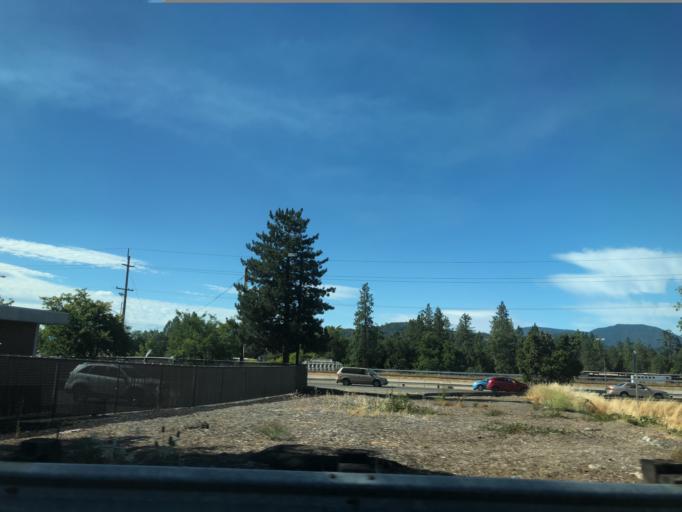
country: US
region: Oregon
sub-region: Josephine County
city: Grants Pass
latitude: 42.4220
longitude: -123.3488
